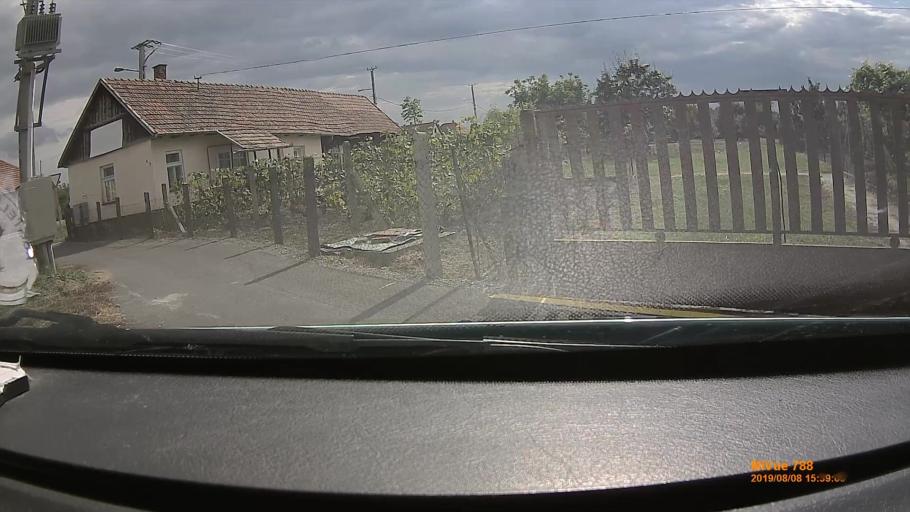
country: HU
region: Szabolcs-Szatmar-Bereg
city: Kocsord
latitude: 47.9385
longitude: 22.4287
